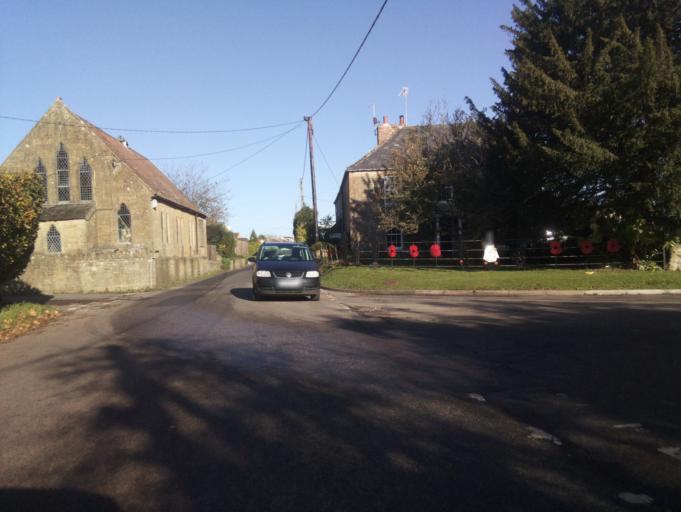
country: GB
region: England
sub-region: Somerset
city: Yeovil
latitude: 50.9189
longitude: -2.6173
